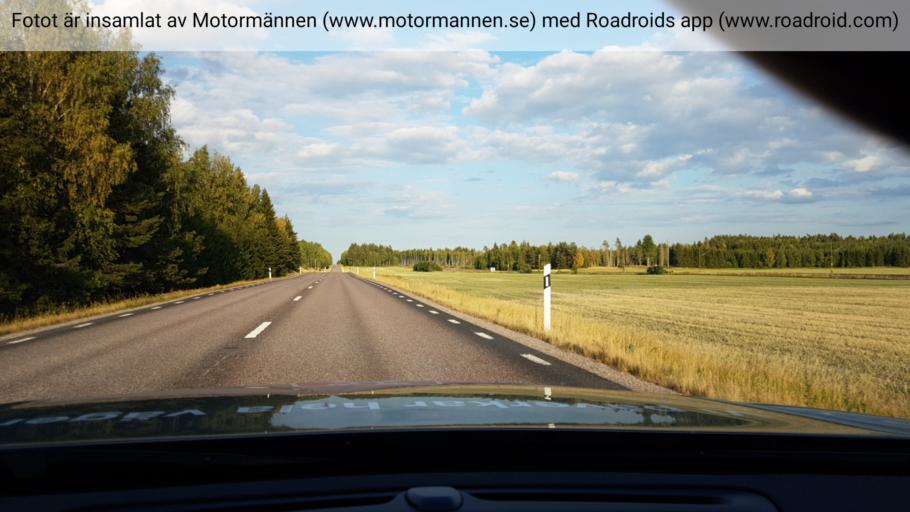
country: SE
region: Uppsala
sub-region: Enkopings Kommun
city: Orsundsbro
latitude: 59.8711
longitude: 17.3064
